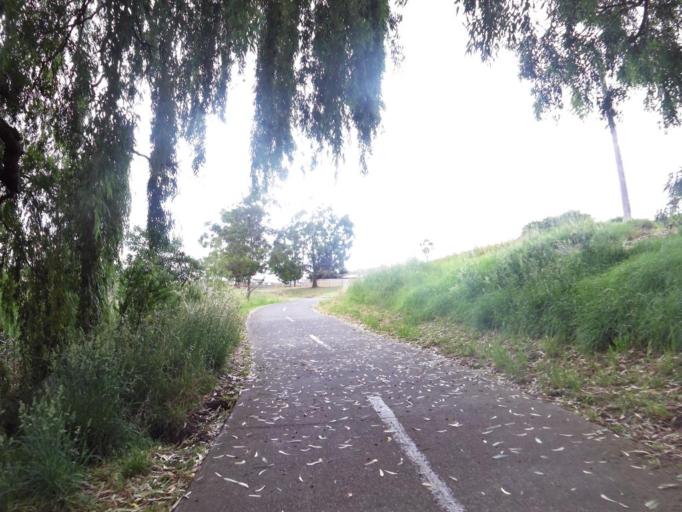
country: AU
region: Victoria
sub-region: Darebin
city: Kingsbury
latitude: -37.7147
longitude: 145.0258
